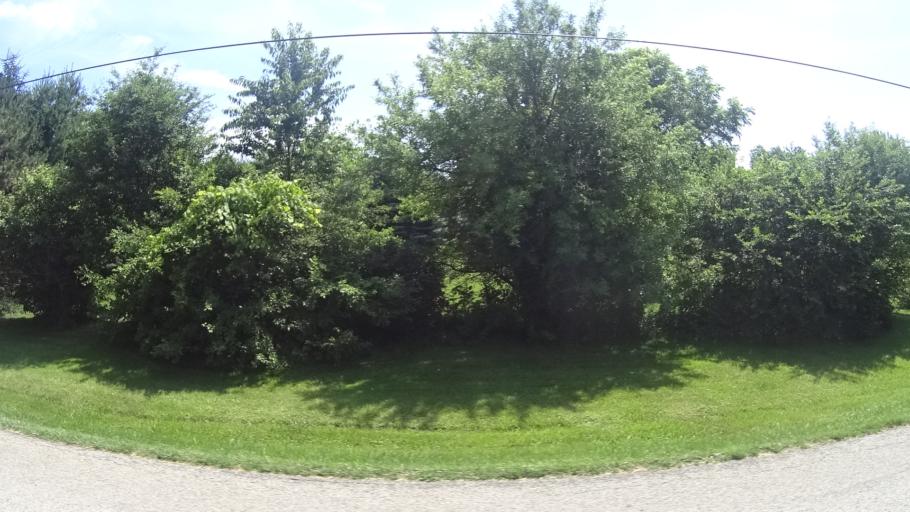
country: US
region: Ohio
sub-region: Huron County
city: Wakeman
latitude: 41.3422
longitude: -82.4591
